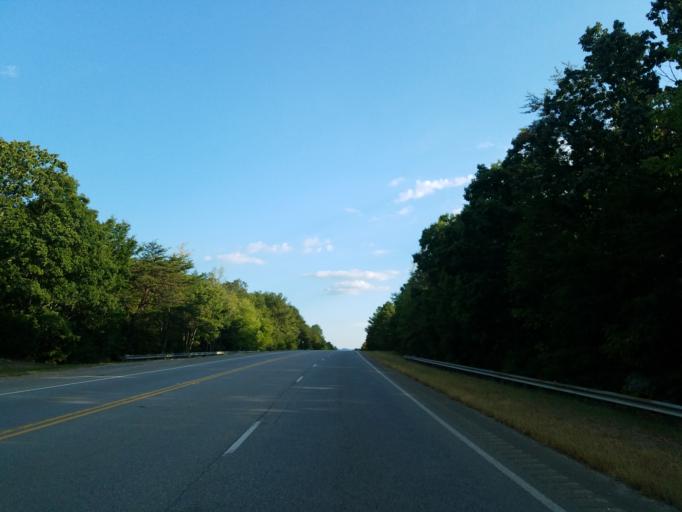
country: US
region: Georgia
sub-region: Murray County
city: Chatsworth
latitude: 34.6849
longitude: -84.7298
